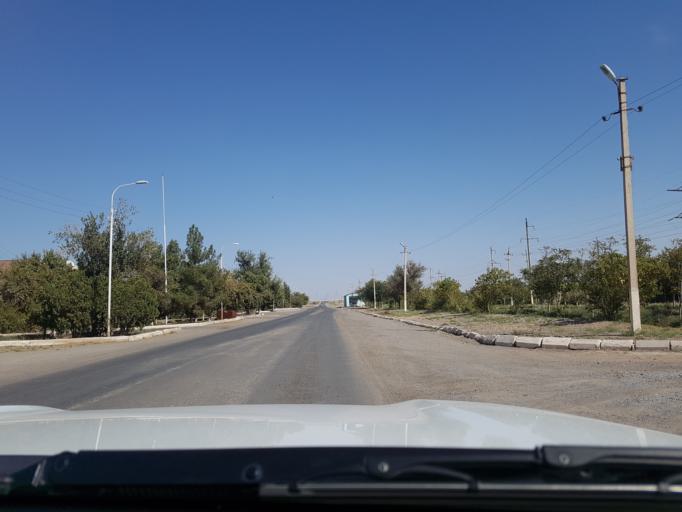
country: IR
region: Razavi Khorasan
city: Sarakhs
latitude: 36.5238
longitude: 61.2248
